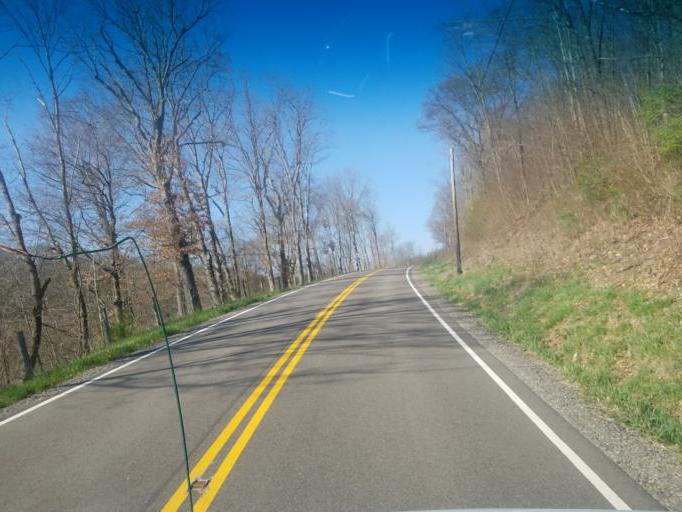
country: US
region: Ohio
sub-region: Muskingum County
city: Frazeysburg
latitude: 40.2481
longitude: -82.1269
